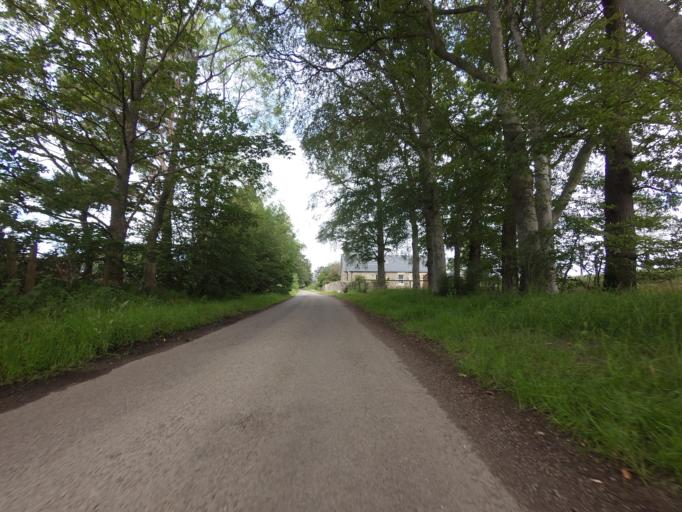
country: GB
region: Scotland
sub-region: Moray
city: Hopeman
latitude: 57.6724
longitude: -3.4006
